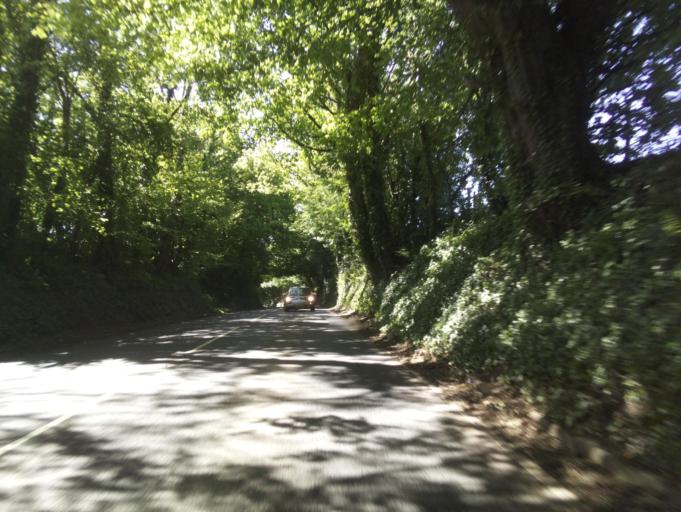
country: GB
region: England
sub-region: Somerset
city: Chard
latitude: 50.8756
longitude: -2.9826
